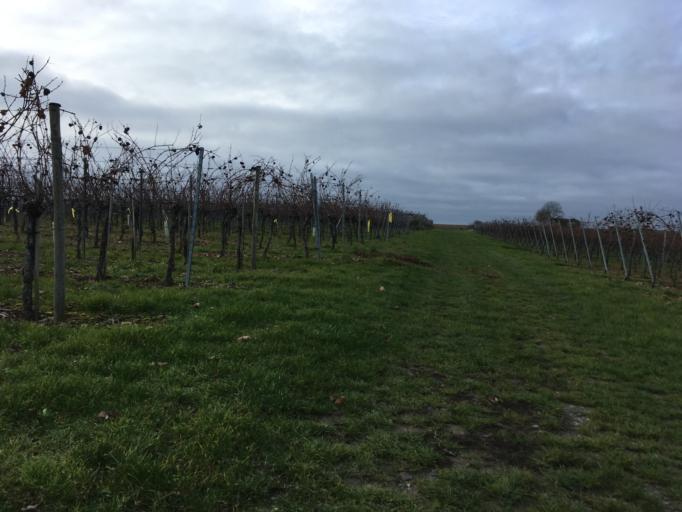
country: DE
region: Baden-Wuerttemberg
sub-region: Regierungsbezirk Stuttgart
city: Lauffen am Neckar
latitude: 49.0820
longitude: 9.1423
